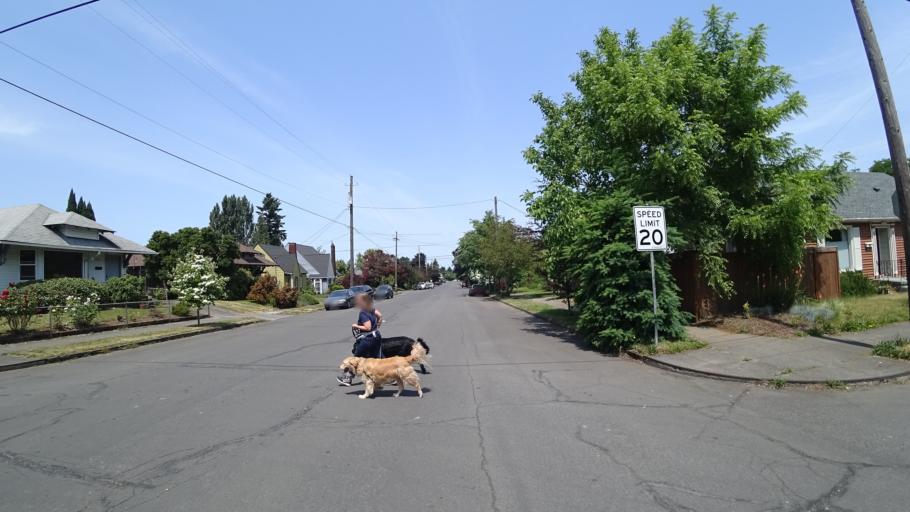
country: US
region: Oregon
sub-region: Multnomah County
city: Portland
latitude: 45.5780
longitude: -122.6743
